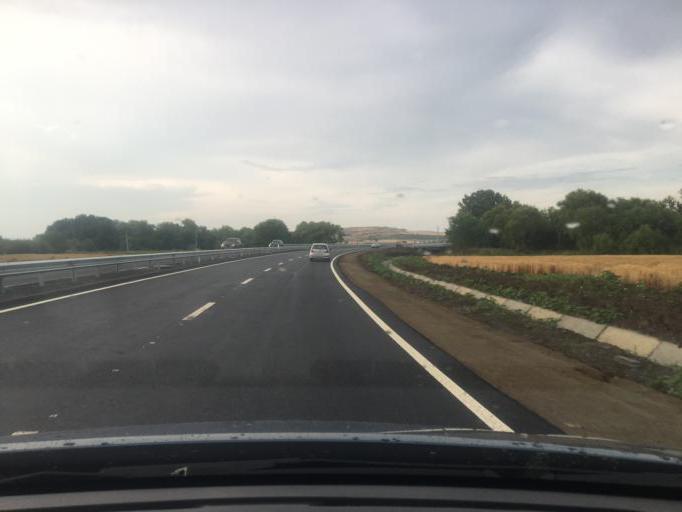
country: BG
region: Burgas
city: Aheloy
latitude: 42.6505
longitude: 27.6371
